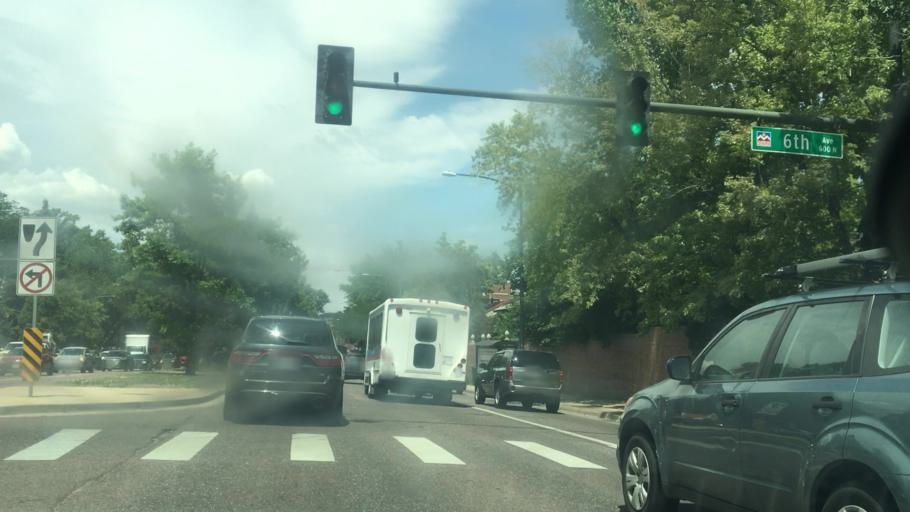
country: US
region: Colorado
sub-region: Arapahoe County
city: Glendale
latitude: 39.7257
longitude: -104.9407
